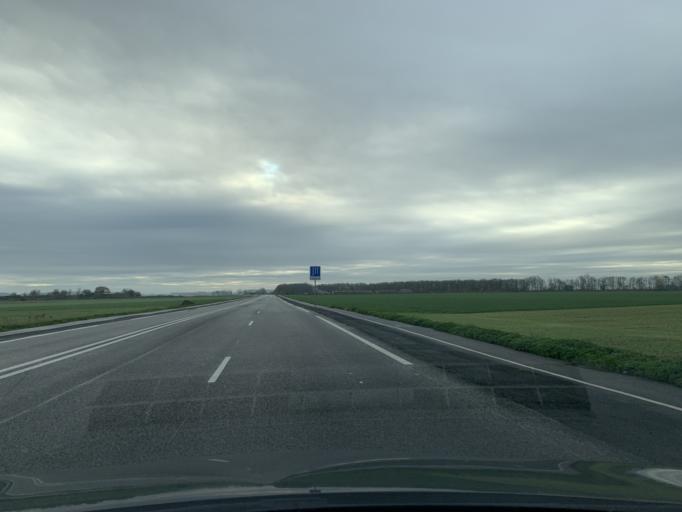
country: FR
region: Nord-Pas-de-Calais
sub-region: Departement du Nord
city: Goeulzin
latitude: 50.3347
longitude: 3.1020
